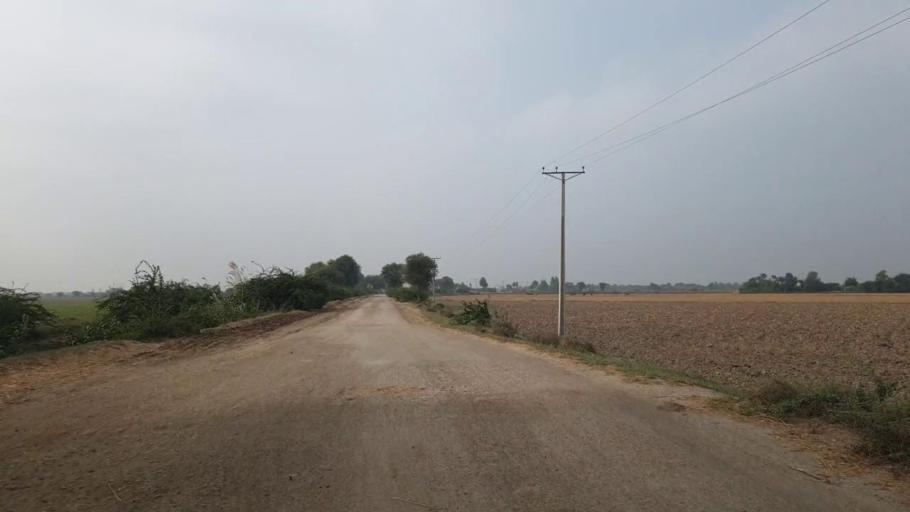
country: PK
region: Sindh
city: Matli
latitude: 24.9660
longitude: 68.5934
